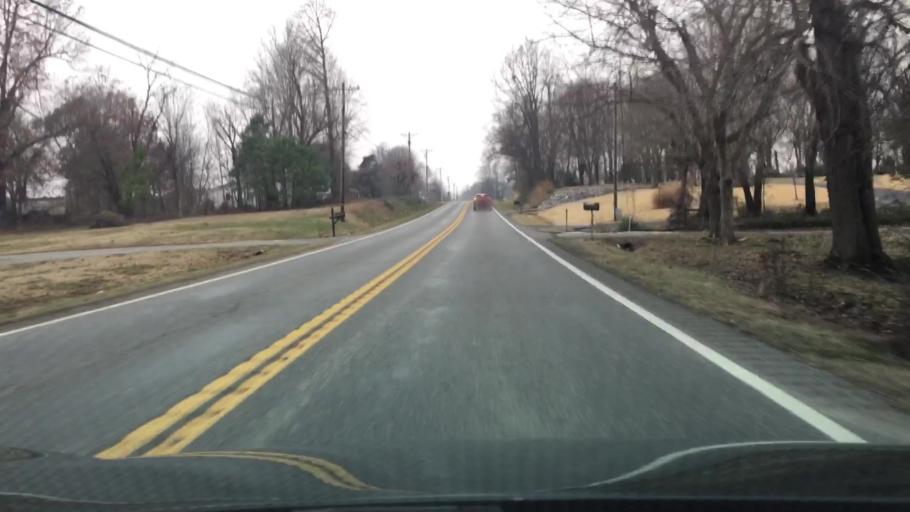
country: US
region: Kentucky
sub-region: Livingston County
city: Ledbetter
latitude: 36.9721
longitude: -88.4654
